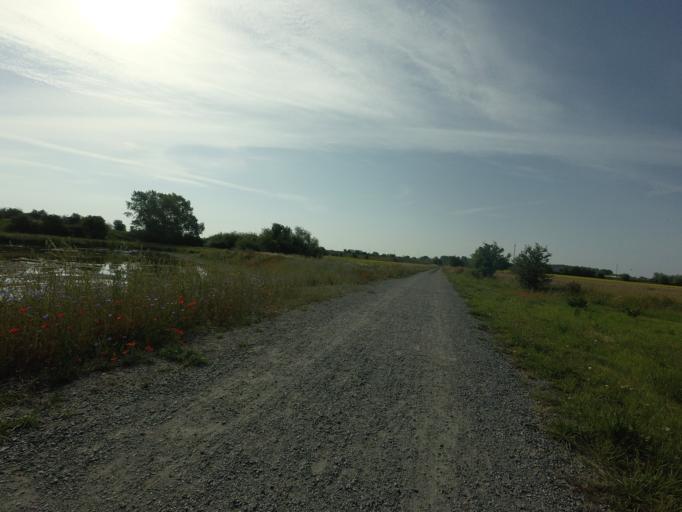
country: SE
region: Skane
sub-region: Vellinge Kommun
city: Vellinge
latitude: 55.4864
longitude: 13.0154
